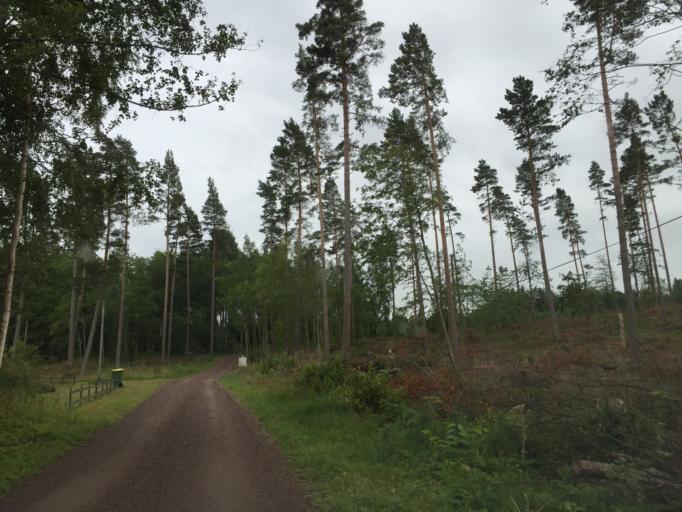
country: SE
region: OEstergoetland
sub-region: Vadstena Kommun
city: Vadstena
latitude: 58.4740
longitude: 14.8316
